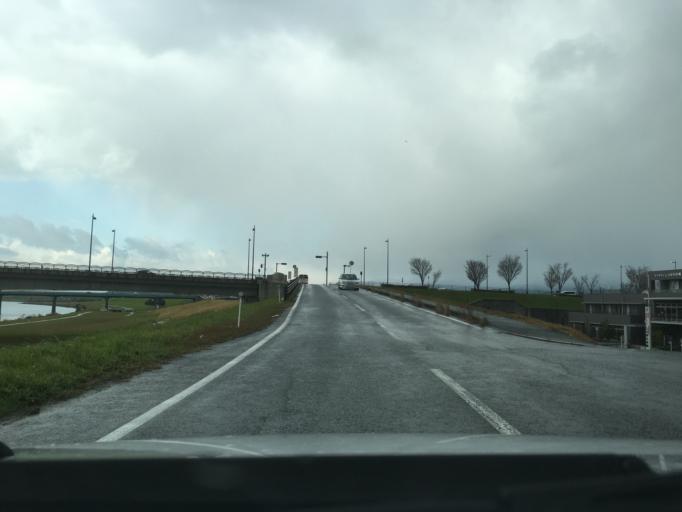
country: JP
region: Fukuoka
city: Kurume
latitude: 33.3335
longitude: 130.5160
